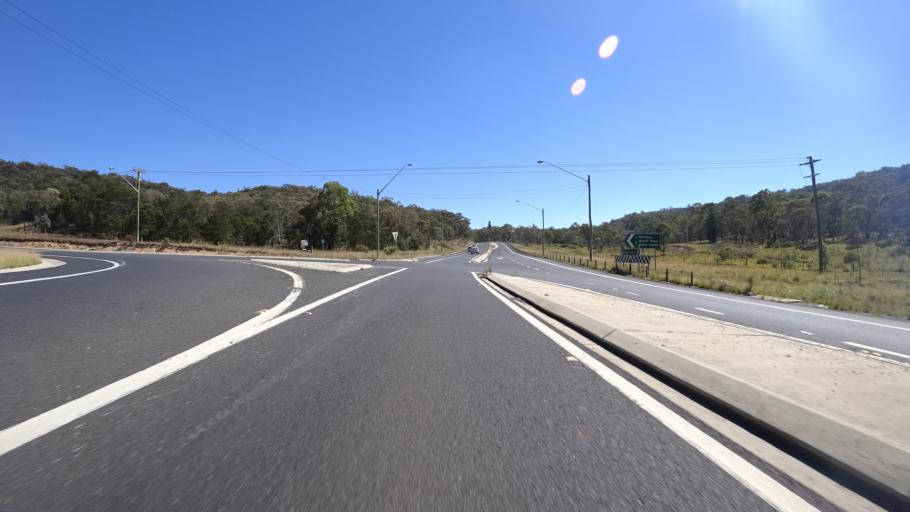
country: AU
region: New South Wales
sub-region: Lithgow
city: Portland
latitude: -33.3482
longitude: 150.0381
